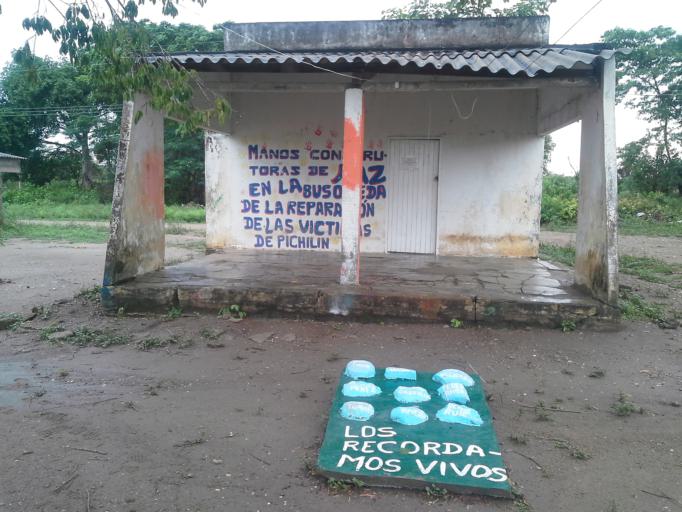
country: CO
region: Sucre
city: Coloso
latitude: 9.4563
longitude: -75.3274
